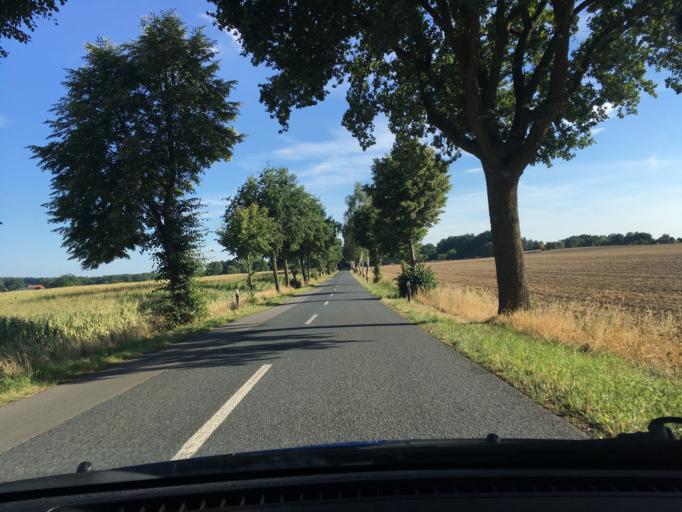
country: DE
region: Lower Saxony
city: Thomasburg
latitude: 53.2321
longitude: 10.7037
